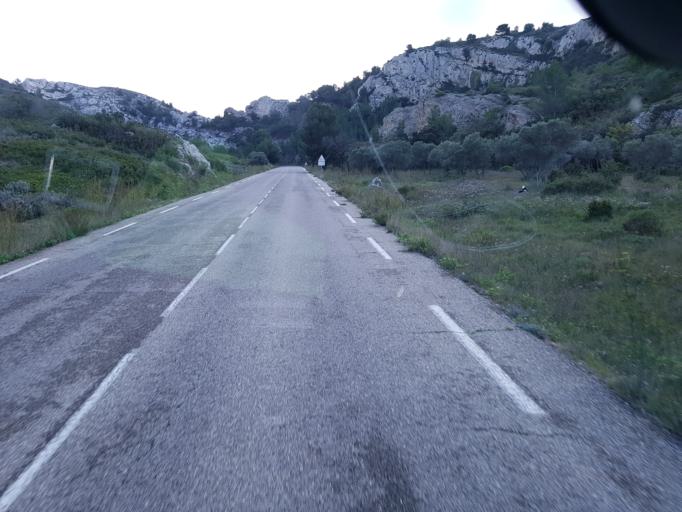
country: FR
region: Provence-Alpes-Cote d'Azur
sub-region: Departement des Bouches-du-Rhone
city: Le Rove
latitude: 43.3545
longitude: 5.2339
